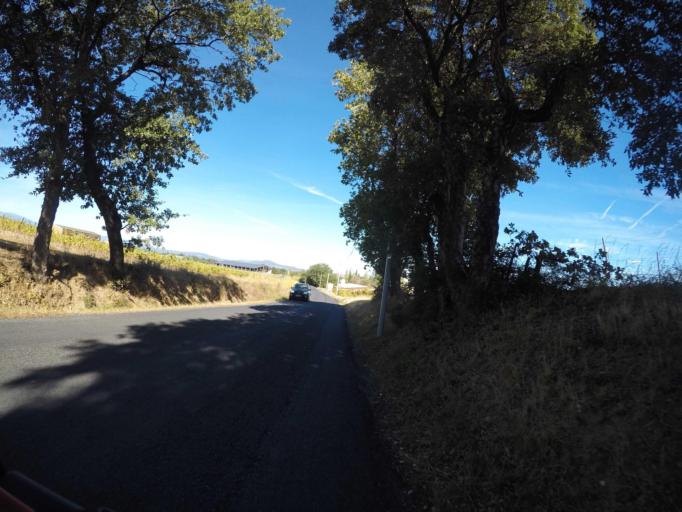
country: FR
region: Languedoc-Roussillon
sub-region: Departement des Pyrenees-Orientales
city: Ponteilla
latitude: 42.6379
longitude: 2.8074
